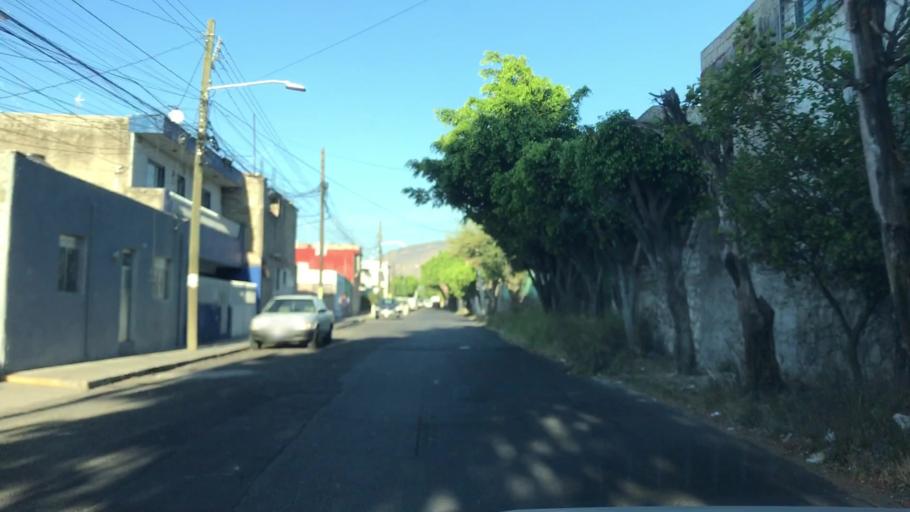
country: MX
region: Jalisco
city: Guadalajara
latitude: 20.6476
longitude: -103.4372
